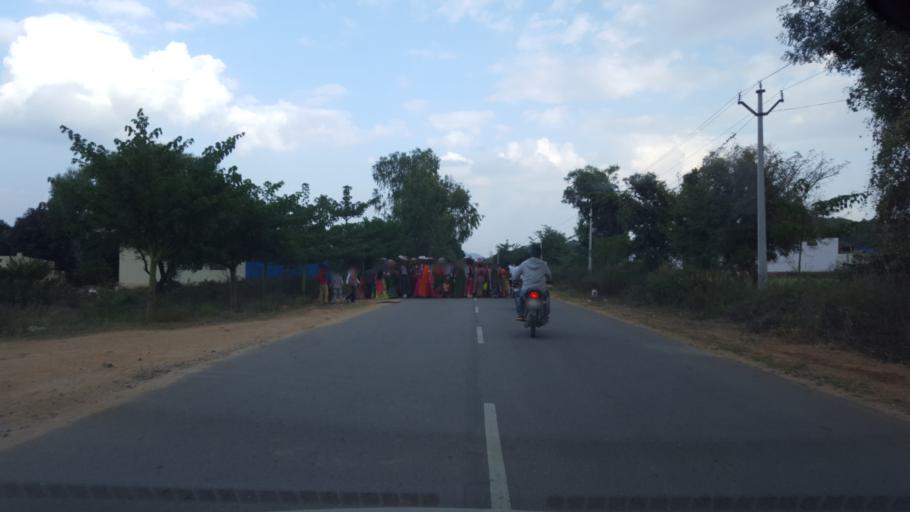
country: IN
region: Telangana
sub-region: Mahbubnagar
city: Mahbubnagar
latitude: 16.7597
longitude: 77.9591
